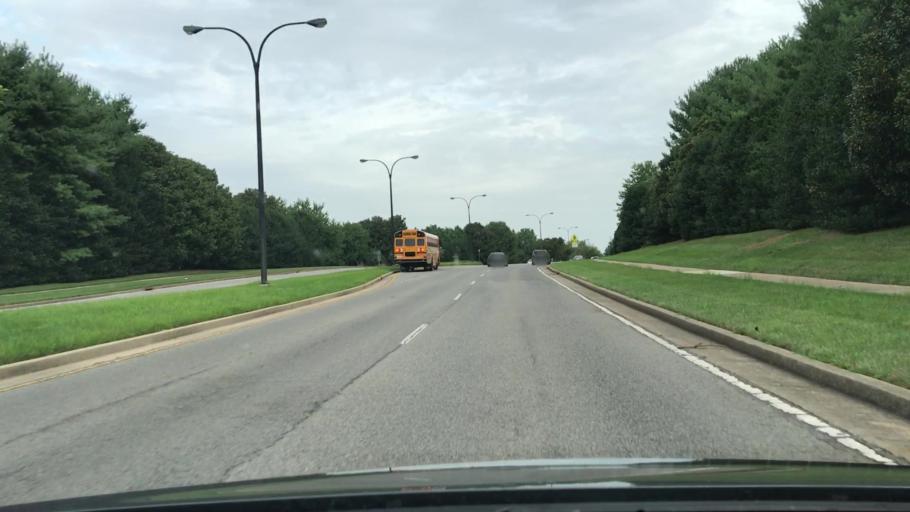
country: US
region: Tennessee
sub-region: Williamson County
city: Franklin
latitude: 35.9420
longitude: -86.7992
